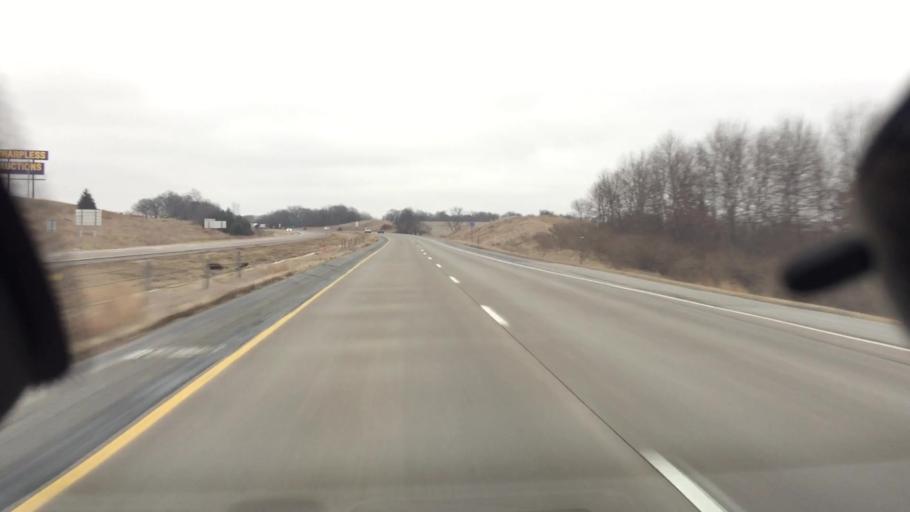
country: US
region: Iowa
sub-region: Cedar County
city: West Branch
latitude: 41.6760
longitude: -91.4373
